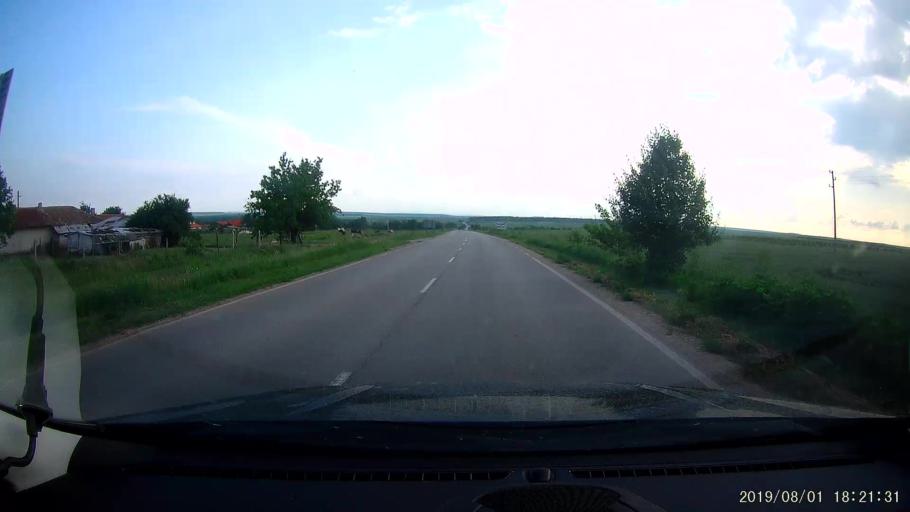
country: BG
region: Shumen
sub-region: Obshtina Kaolinovo
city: Kaolinovo
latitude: 43.6522
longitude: 27.0706
